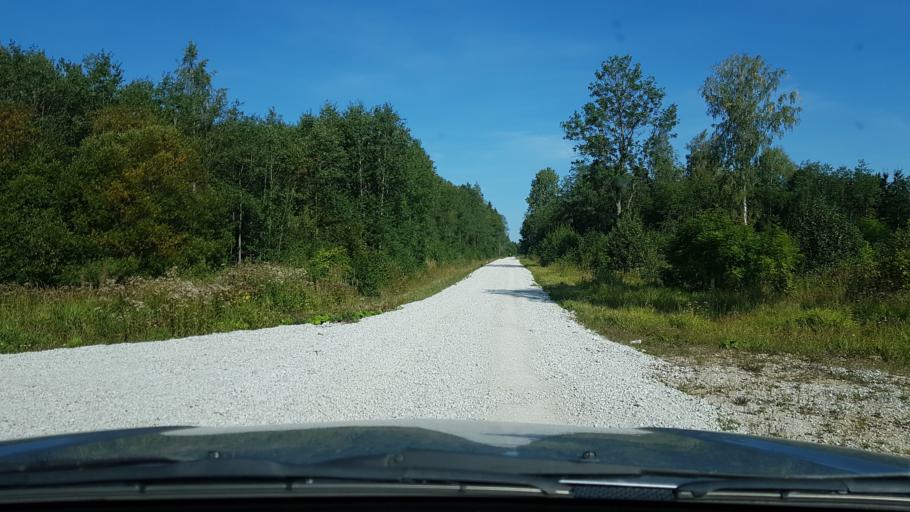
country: EE
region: Ida-Virumaa
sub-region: Sillamaee linn
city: Sillamae
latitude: 59.3358
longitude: 27.7328
